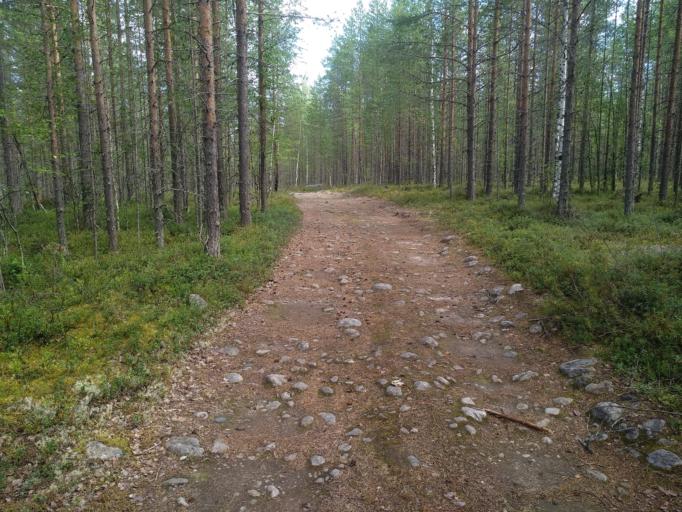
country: RU
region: Republic of Karelia
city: Kalevala
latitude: 64.9864
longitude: 31.2159
